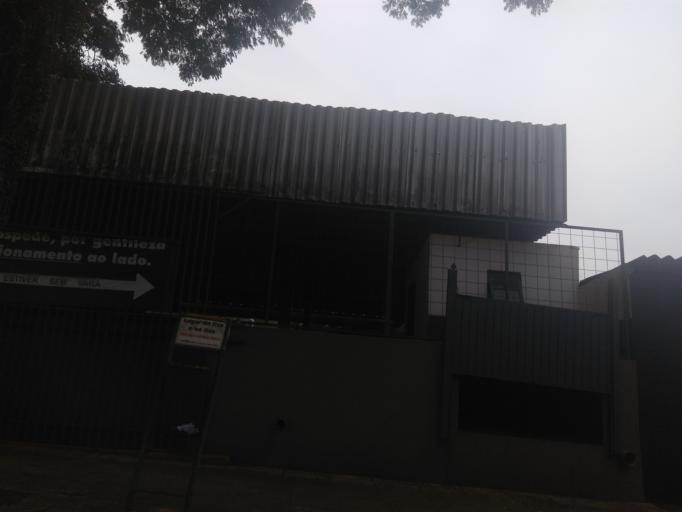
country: BR
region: Mato Grosso do Sul
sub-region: Dourados
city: Dourados
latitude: -22.2270
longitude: -54.8117
